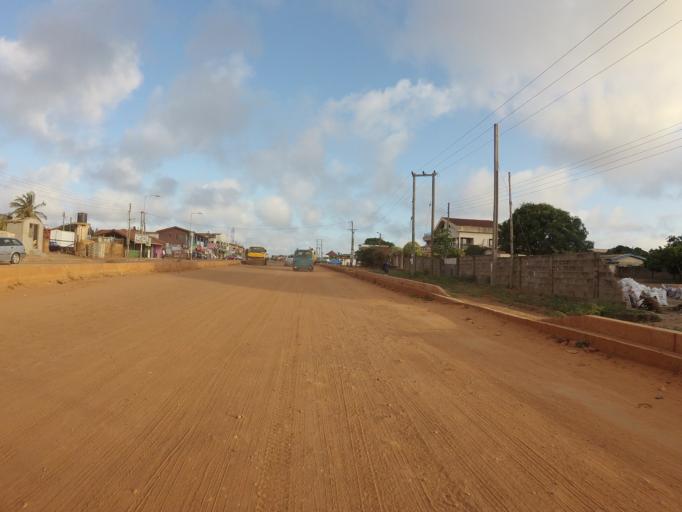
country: GH
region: Greater Accra
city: Teshi Old Town
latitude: 5.5980
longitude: -0.1188
